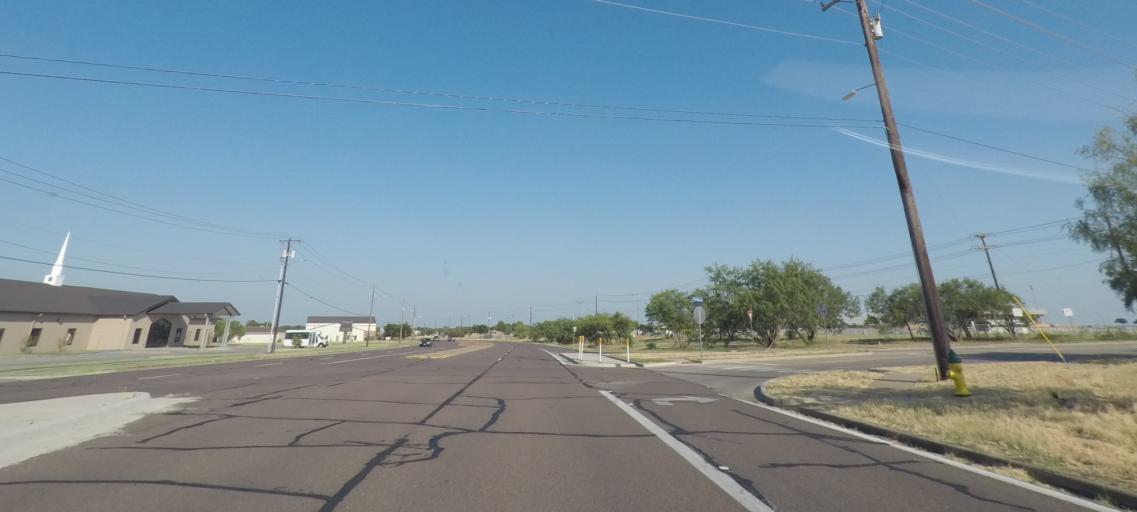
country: US
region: Texas
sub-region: Wichita County
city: Wichita Falls
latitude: 33.8587
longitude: -98.5865
